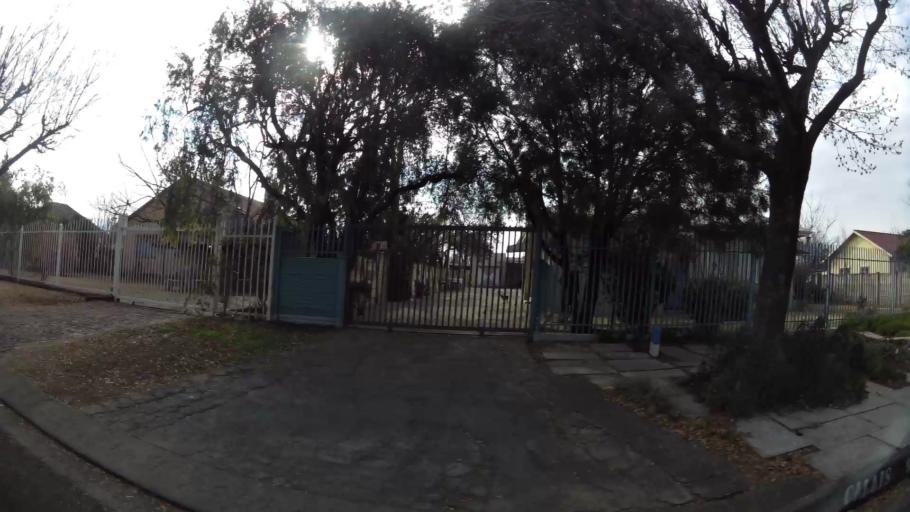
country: ZA
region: Orange Free State
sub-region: Mangaung Metropolitan Municipality
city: Bloemfontein
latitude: -29.0820
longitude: 26.2424
